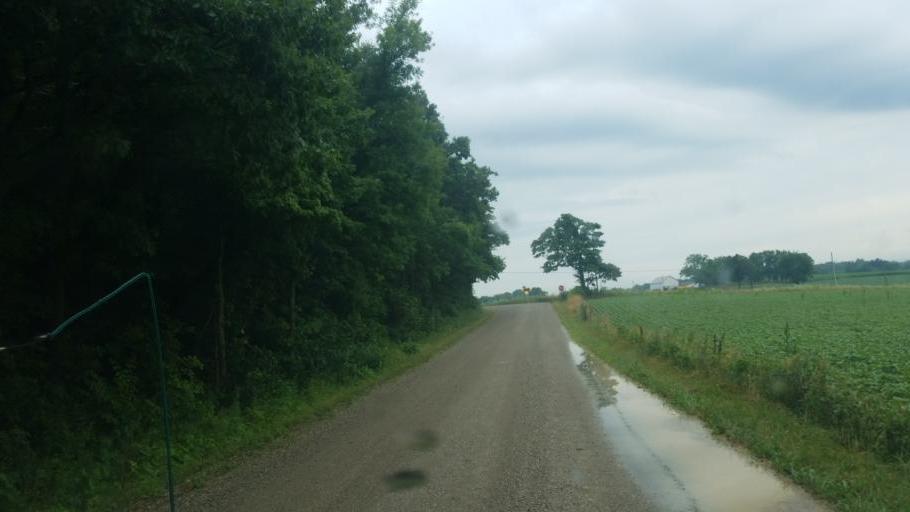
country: US
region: Indiana
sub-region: Steuben County
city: Hamilton
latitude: 41.5156
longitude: -84.9331
